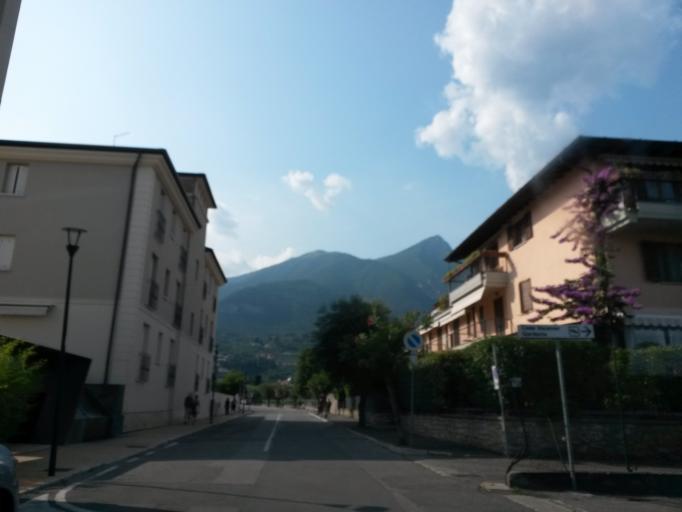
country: IT
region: Lombardy
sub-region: Provincia di Brescia
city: Toscolano Maderno
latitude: 45.6320
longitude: 10.6119
